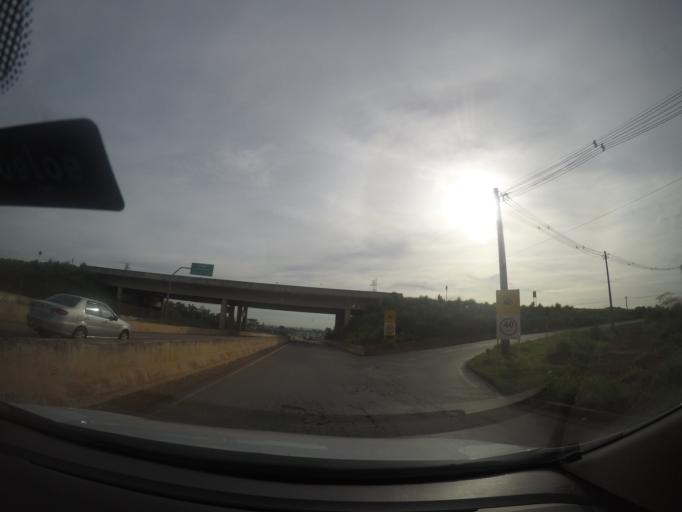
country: BR
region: Goias
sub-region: Goiania
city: Goiania
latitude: -16.7129
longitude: -49.3576
